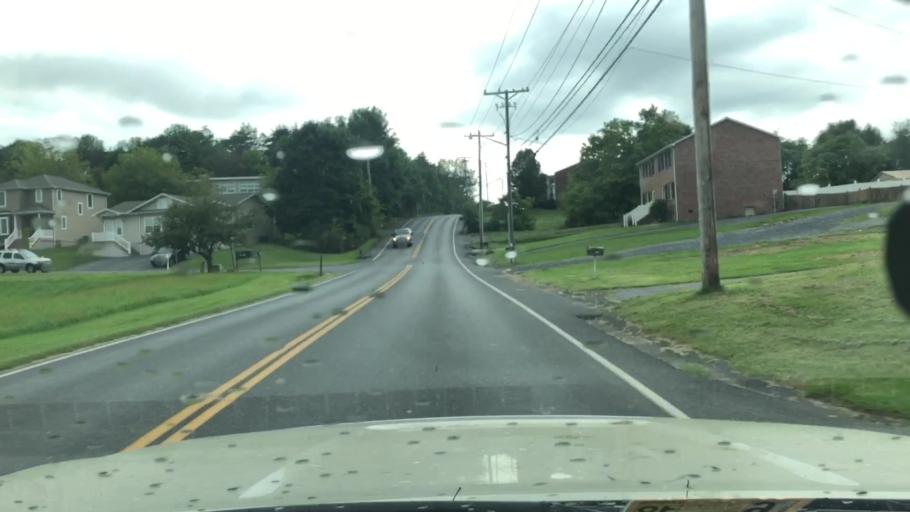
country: US
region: Virginia
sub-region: City of Harrisonburg
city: Harrisonburg
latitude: 38.4291
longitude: -78.8953
